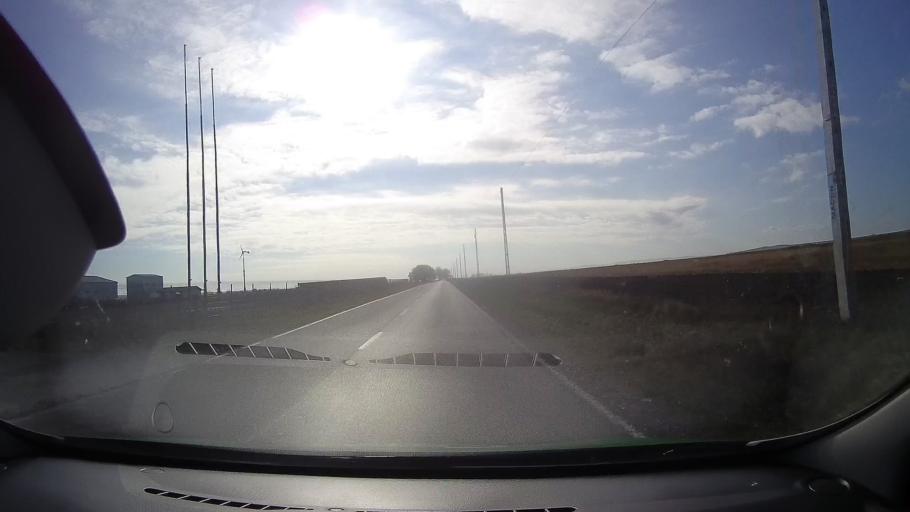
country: RO
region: Tulcea
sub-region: Comuna Valea Nucarilor
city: Agighiol
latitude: 45.0203
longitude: 28.8827
